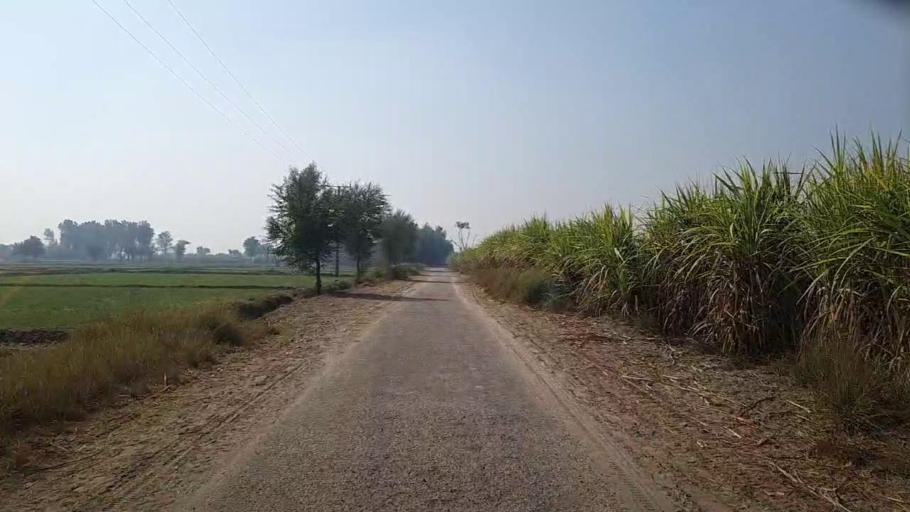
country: PK
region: Sindh
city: Bozdar
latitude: 27.2652
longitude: 68.6232
